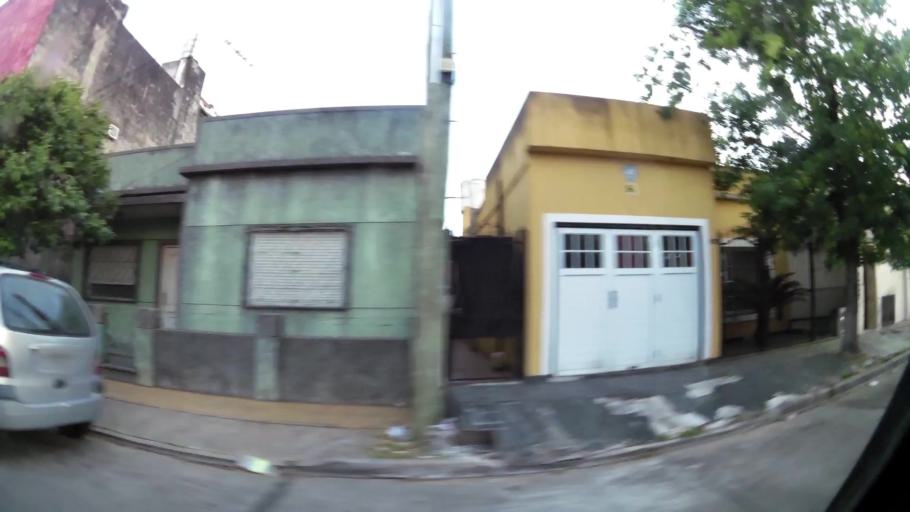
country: AR
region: Buenos Aires
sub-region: Partido de Avellaneda
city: Avellaneda
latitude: -34.6799
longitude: -58.3382
